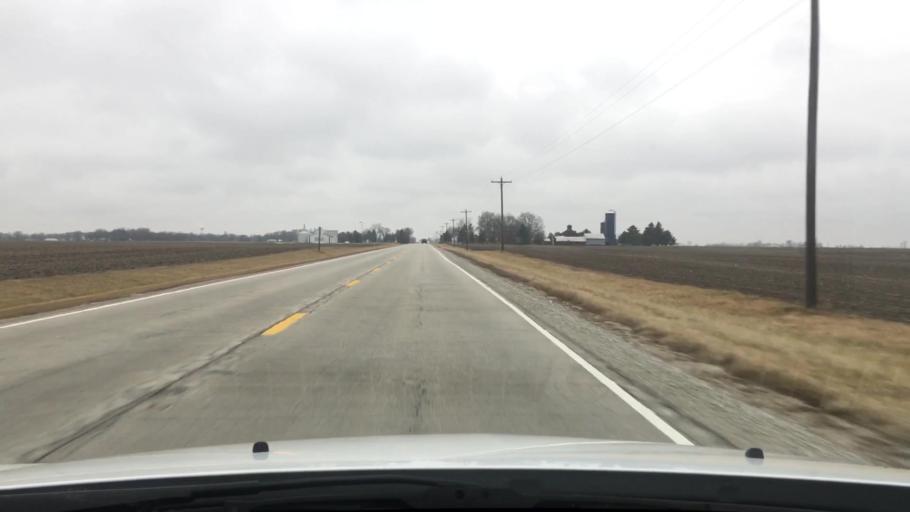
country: US
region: Illinois
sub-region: Iroquois County
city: Clifton
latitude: 40.8855
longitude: -87.9246
